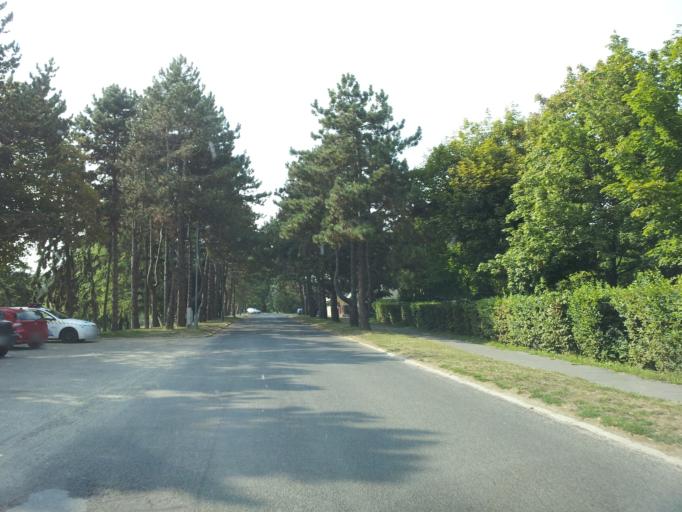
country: HU
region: Vas
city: Szombathely
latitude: 47.2361
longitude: 16.6001
